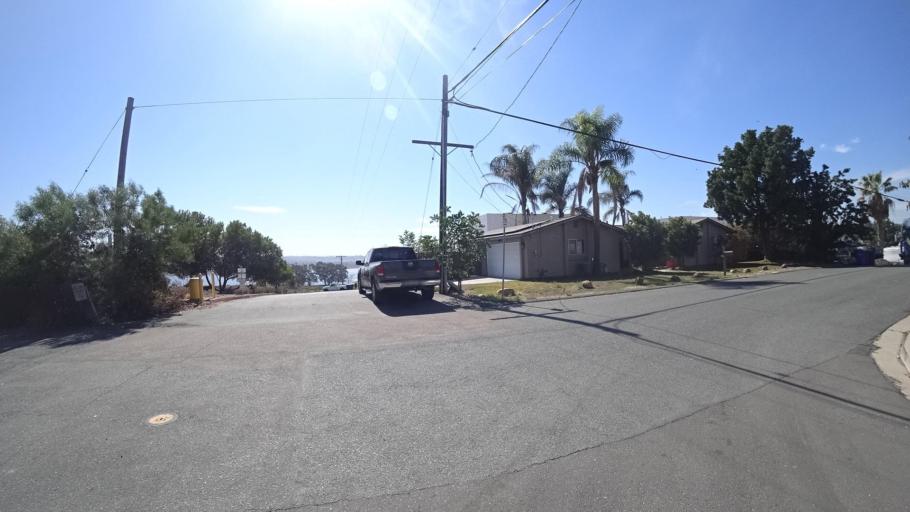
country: US
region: California
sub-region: San Diego County
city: La Presa
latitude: 32.7041
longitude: -116.9935
